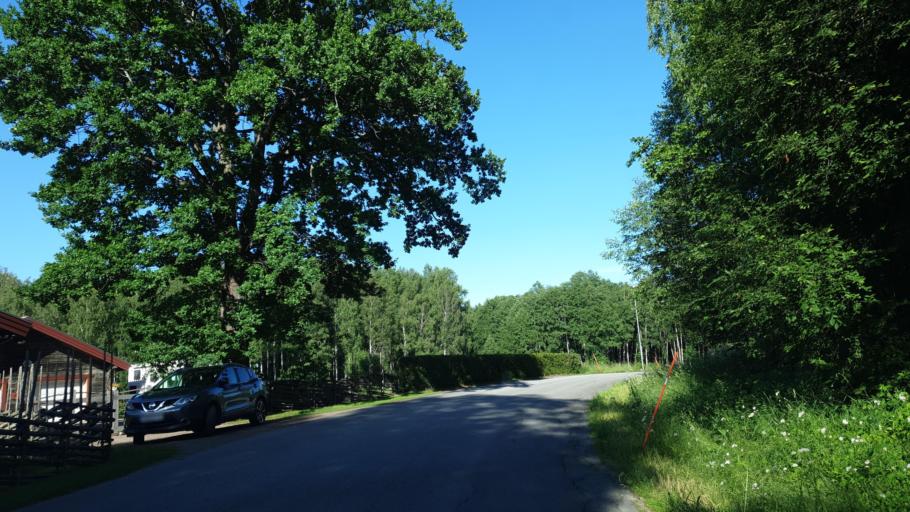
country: SE
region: Dalarna
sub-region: Avesta Kommun
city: Avesta
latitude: 60.1293
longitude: 16.2586
